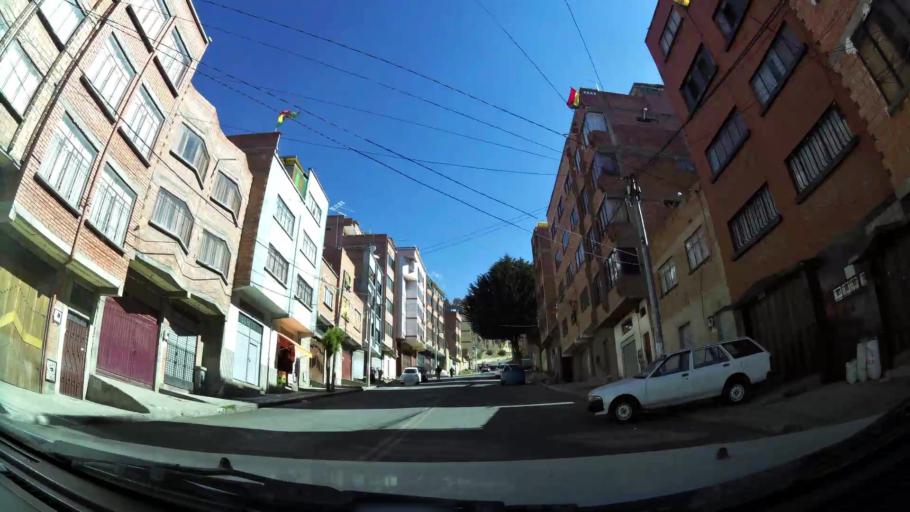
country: BO
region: La Paz
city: La Paz
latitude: -16.5034
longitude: -68.1479
